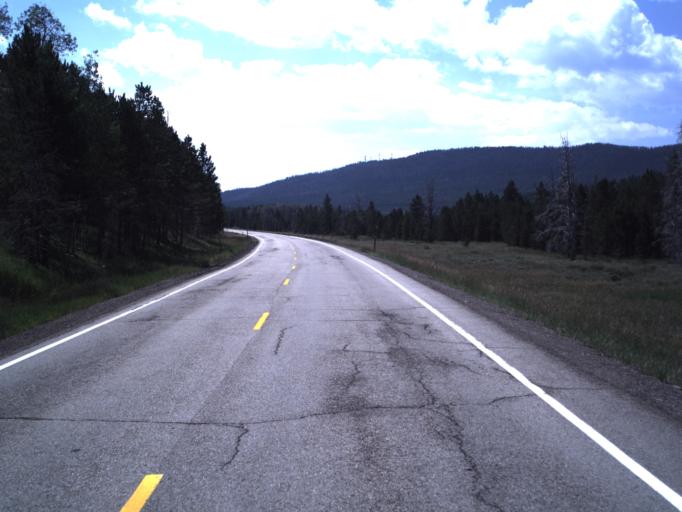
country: US
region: Utah
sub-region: Uintah County
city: Maeser
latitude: 40.7753
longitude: -109.4708
